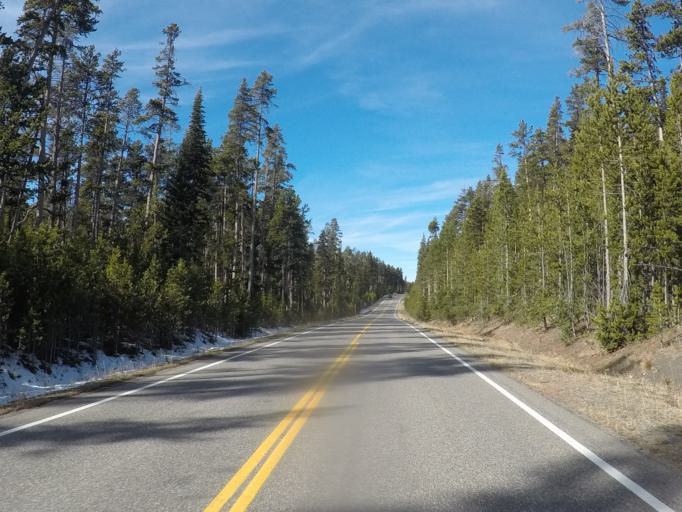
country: US
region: Montana
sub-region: Gallatin County
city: West Yellowstone
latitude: 44.4249
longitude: -110.6158
